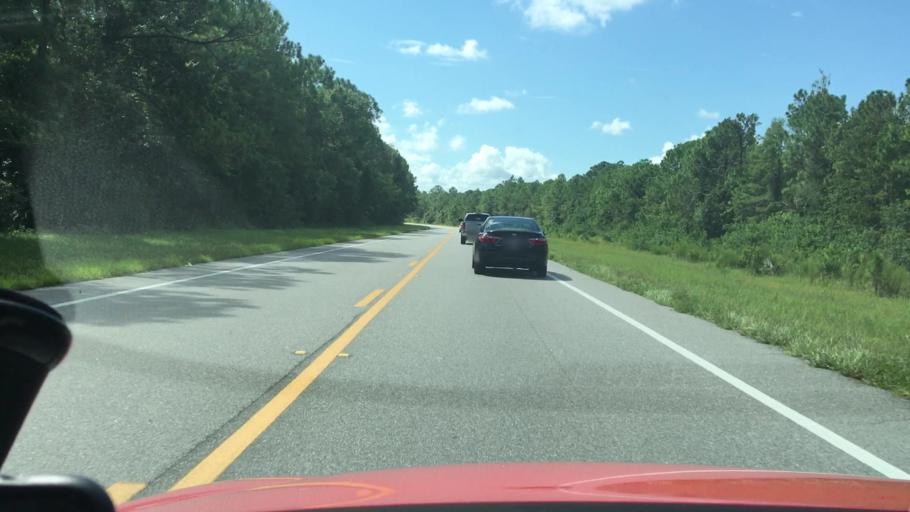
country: US
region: Florida
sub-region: Volusia County
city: South Daytona
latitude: 29.1438
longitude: -81.0591
